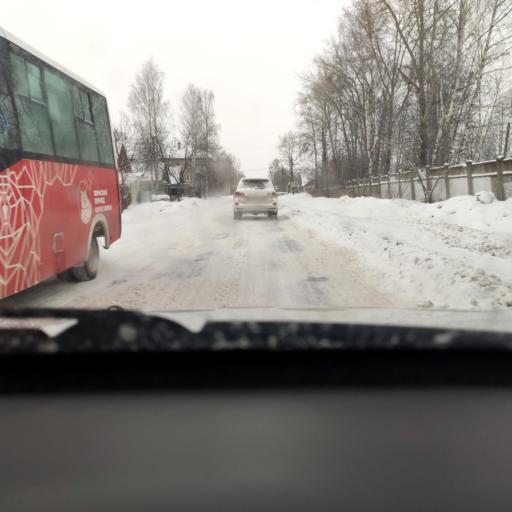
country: RU
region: Perm
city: Polazna
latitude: 58.1482
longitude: 56.4444
